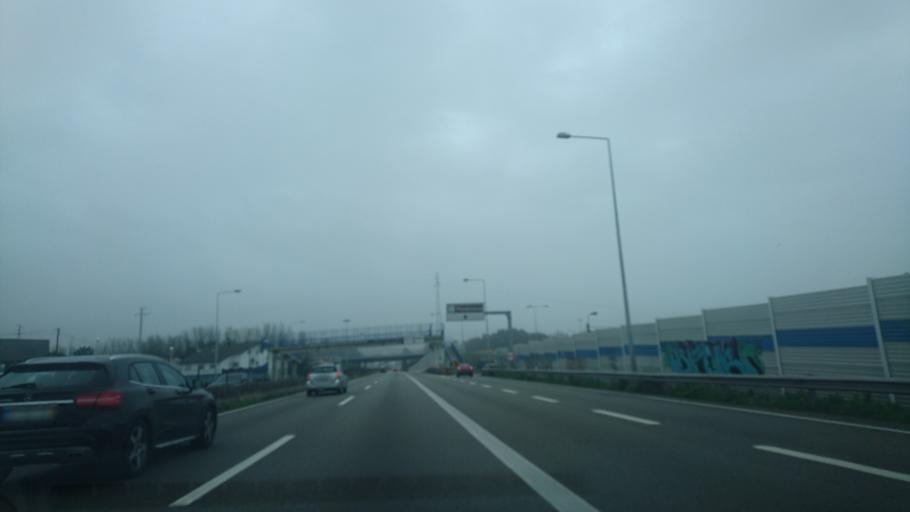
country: PT
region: Porto
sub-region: Vila Nova de Gaia
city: Vilar do Paraiso
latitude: 41.1108
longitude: -8.6260
